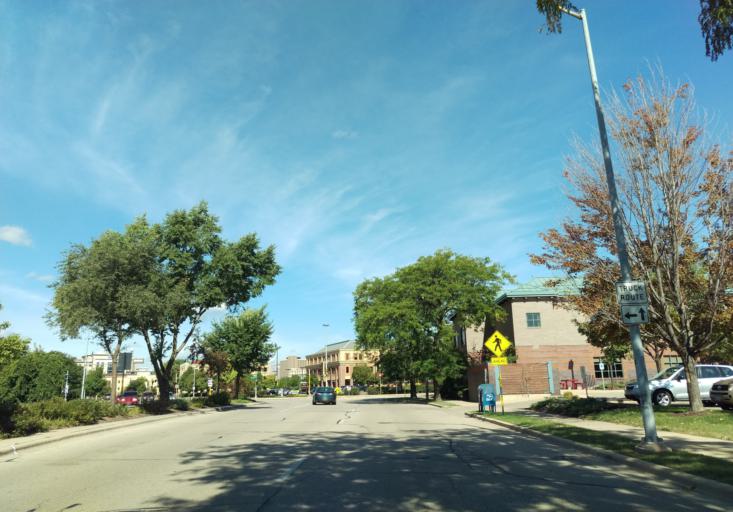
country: US
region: Wisconsin
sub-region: Dane County
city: Madison
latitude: 43.0665
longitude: -89.3940
